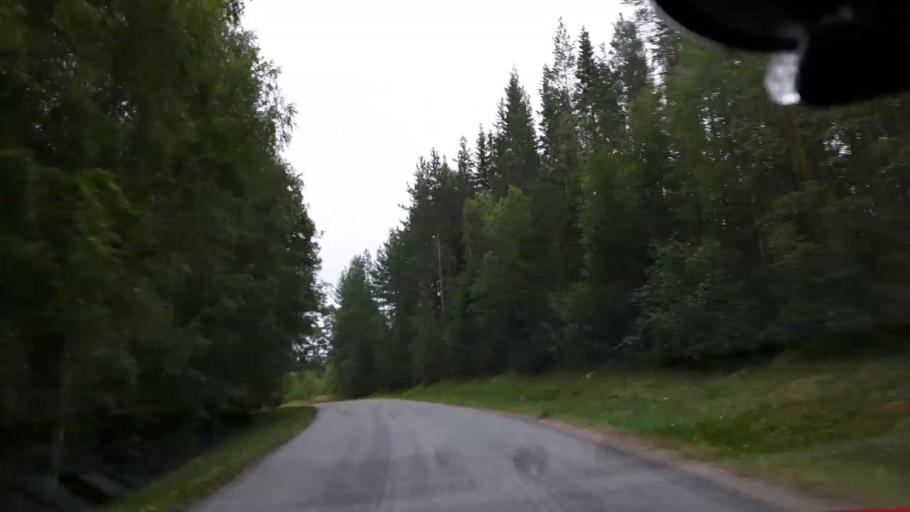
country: SE
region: Vaesternorrland
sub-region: Ange Kommun
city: Fransta
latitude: 62.7693
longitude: 16.0168
